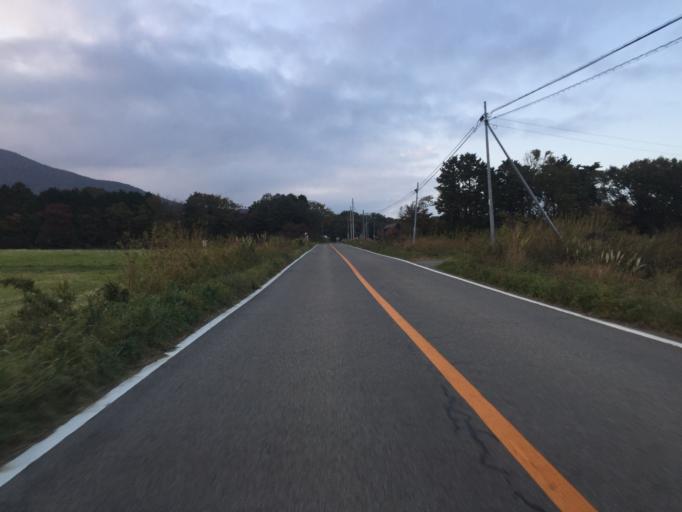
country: JP
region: Fukushima
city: Nihommatsu
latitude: 37.6255
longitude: 140.3522
